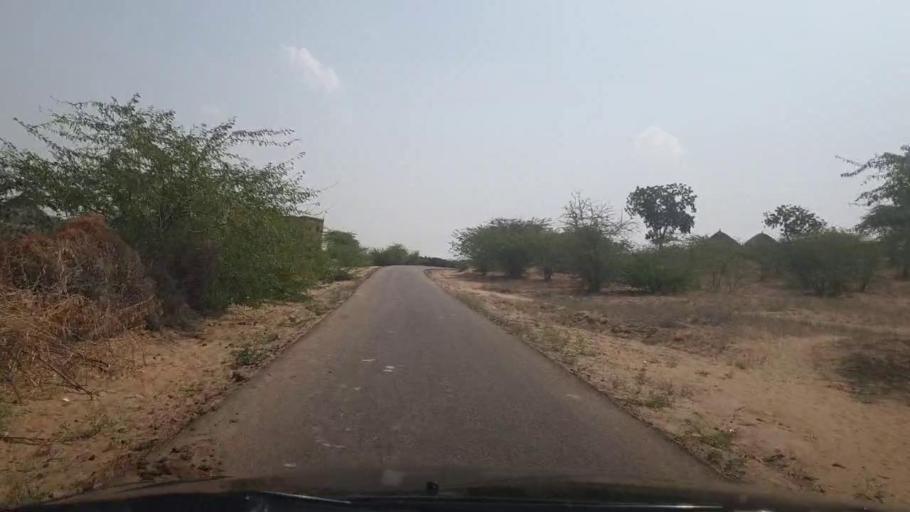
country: PK
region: Sindh
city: Islamkot
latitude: 25.0045
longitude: 70.4155
